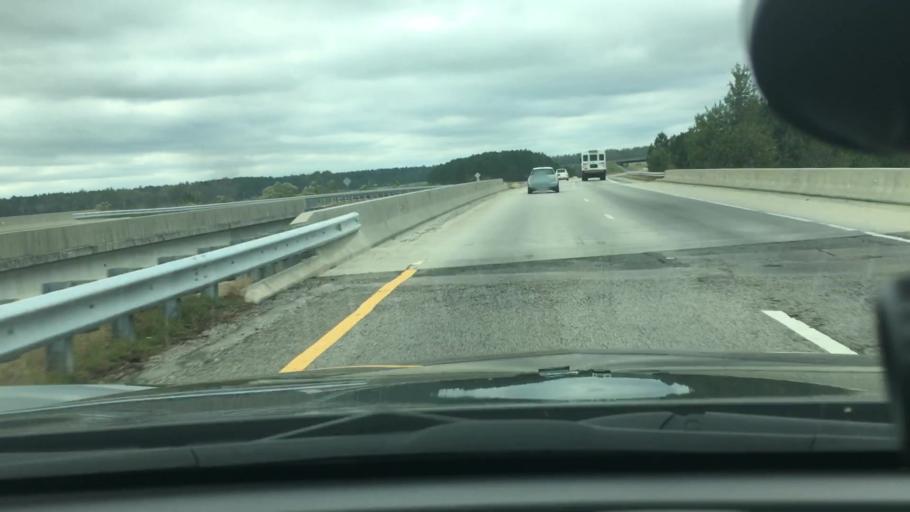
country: US
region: North Carolina
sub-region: Wilson County
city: Wilson
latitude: 35.6691
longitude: -77.8728
